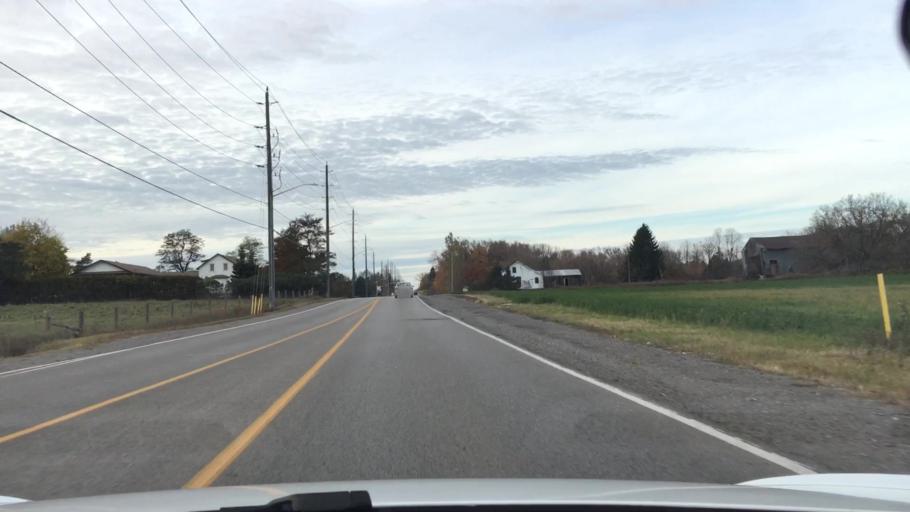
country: CA
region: Ontario
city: Oshawa
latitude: 43.9318
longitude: -78.8244
